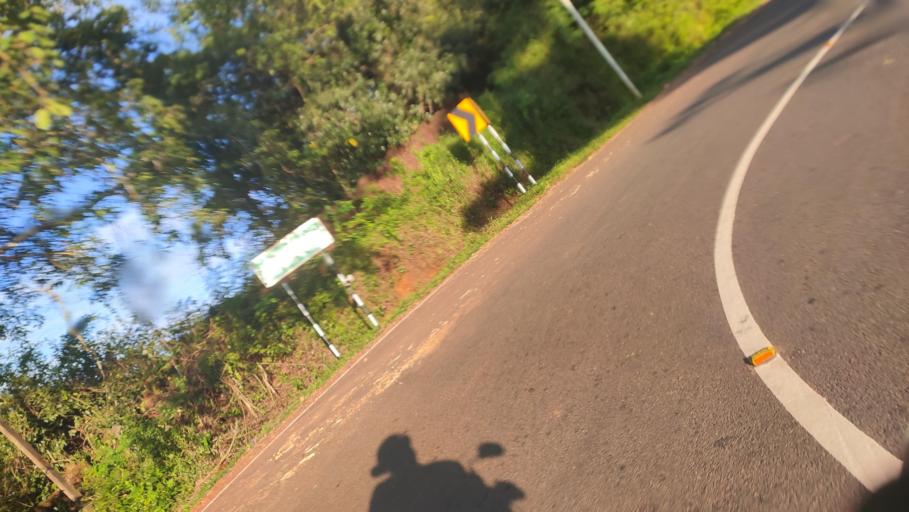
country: IN
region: Kerala
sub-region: Kasaragod District
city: Kasaragod
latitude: 12.4613
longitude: 75.0917
